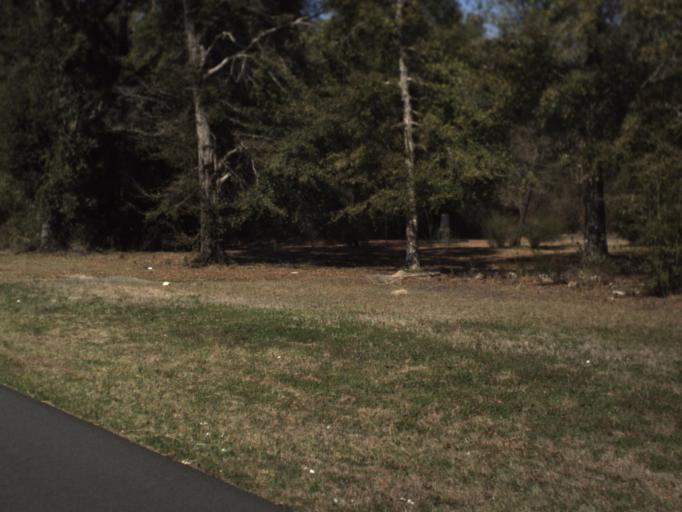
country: US
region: Florida
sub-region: Jackson County
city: Malone
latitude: 30.8584
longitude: -85.0964
